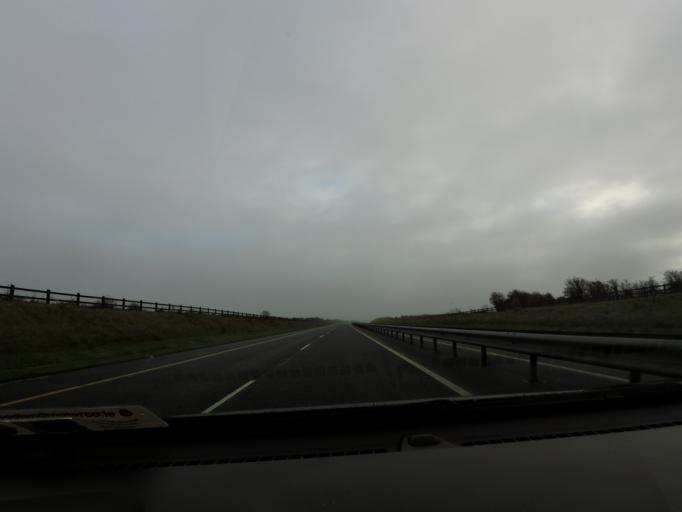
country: IE
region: Connaught
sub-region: County Galway
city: Ballinasloe
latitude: 53.3251
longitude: -8.1392
